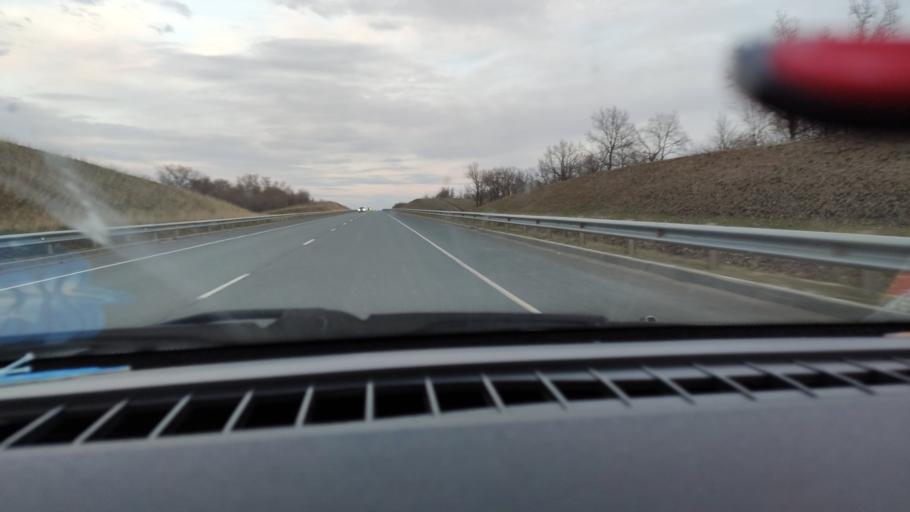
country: RU
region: Saratov
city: Yelshanka
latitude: 51.8215
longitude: 46.3344
